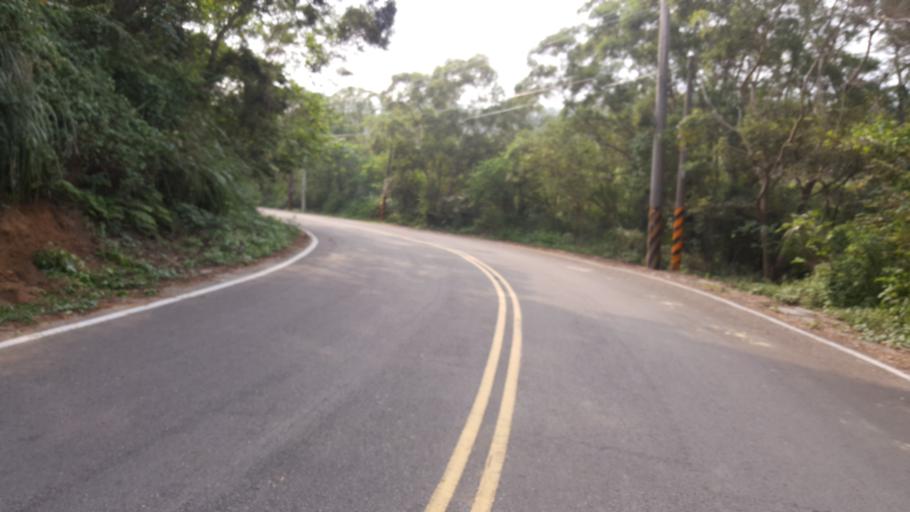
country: TW
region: Taiwan
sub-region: Hsinchu
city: Hsinchu
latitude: 24.7221
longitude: 120.9564
